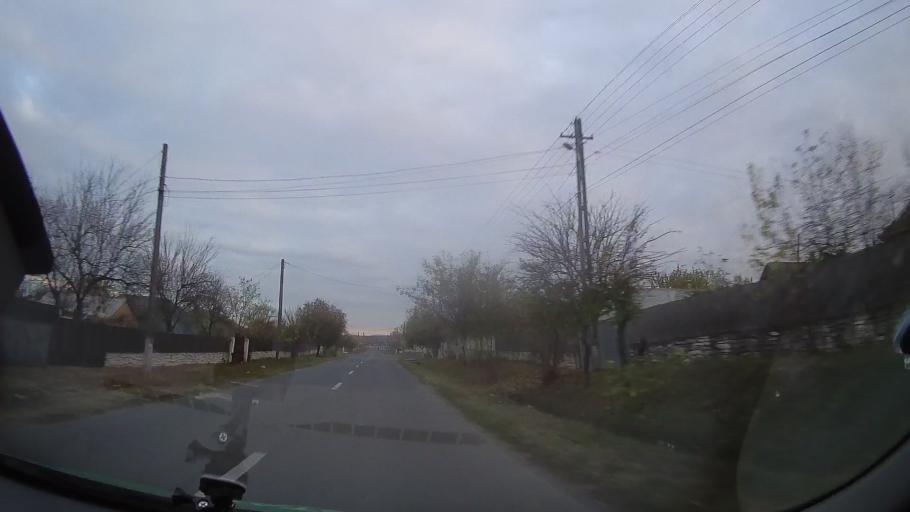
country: RO
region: Tulcea
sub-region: Comuna Mihai Bravu
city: Turda
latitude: 44.9753
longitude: 28.6220
